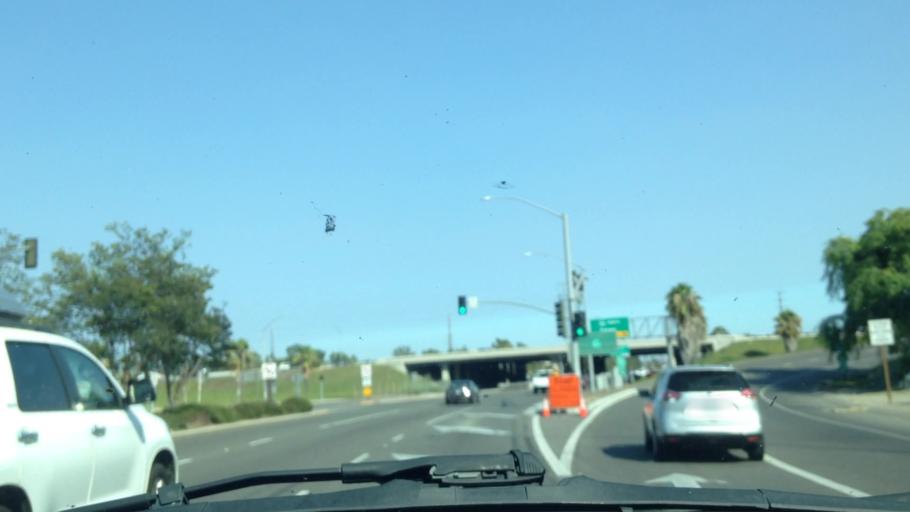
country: US
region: California
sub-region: Orange County
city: Santa Ana
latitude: 33.6996
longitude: -117.8634
